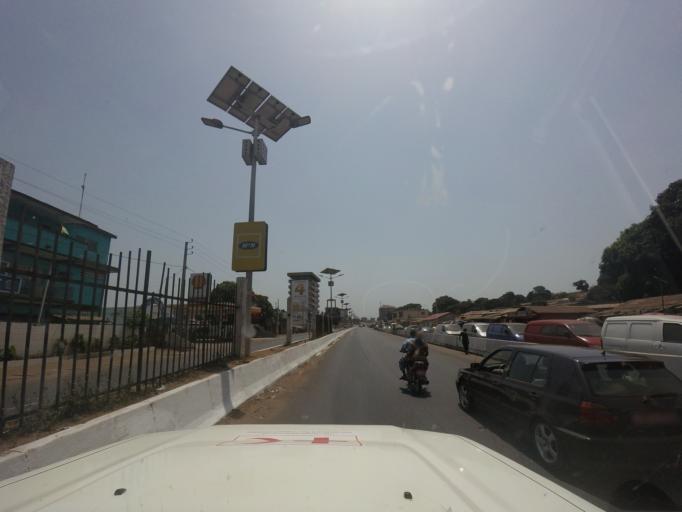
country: GN
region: Conakry
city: Conakry
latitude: 9.5600
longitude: -13.6437
